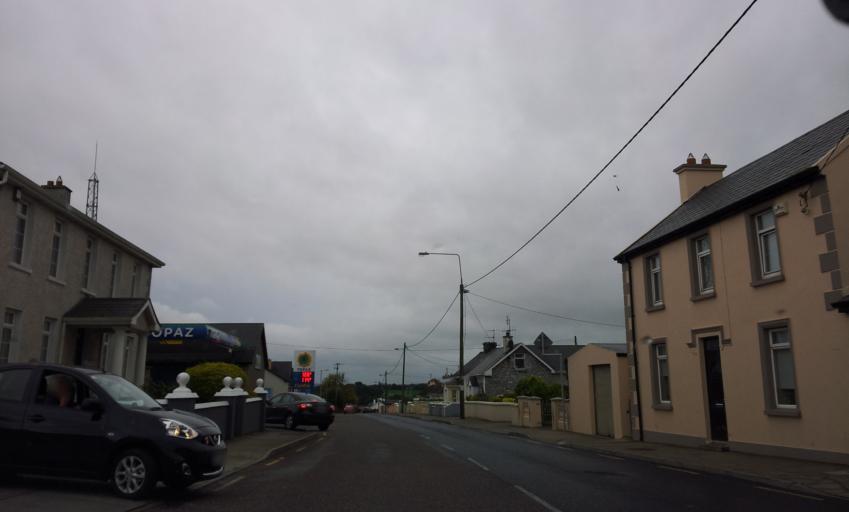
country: IE
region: Munster
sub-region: County Cork
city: Mitchelstown
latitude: 52.2459
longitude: -8.4285
